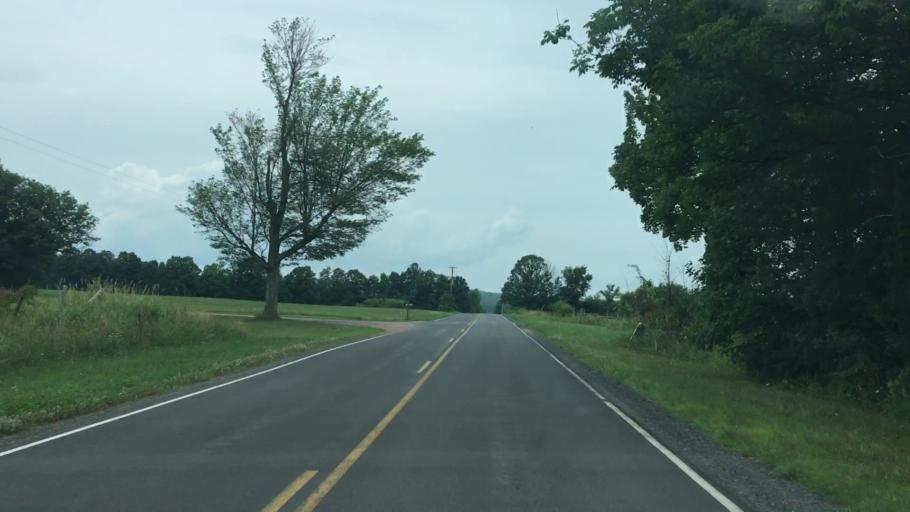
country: US
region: New York
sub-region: Clinton County
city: Peru
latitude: 44.5982
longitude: -73.6277
